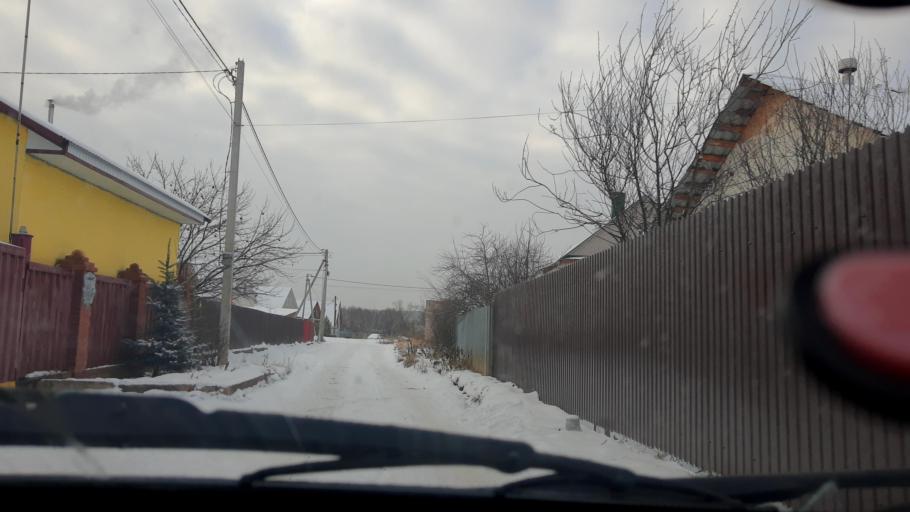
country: RU
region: Bashkortostan
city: Iglino
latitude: 54.7431
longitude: 56.2812
